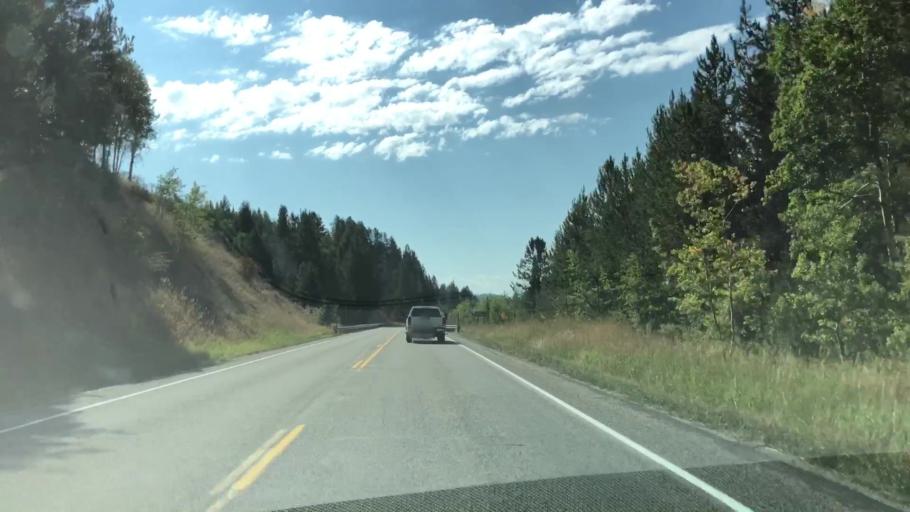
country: US
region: Idaho
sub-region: Teton County
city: Victor
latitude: 43.2903
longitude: -111.1231
